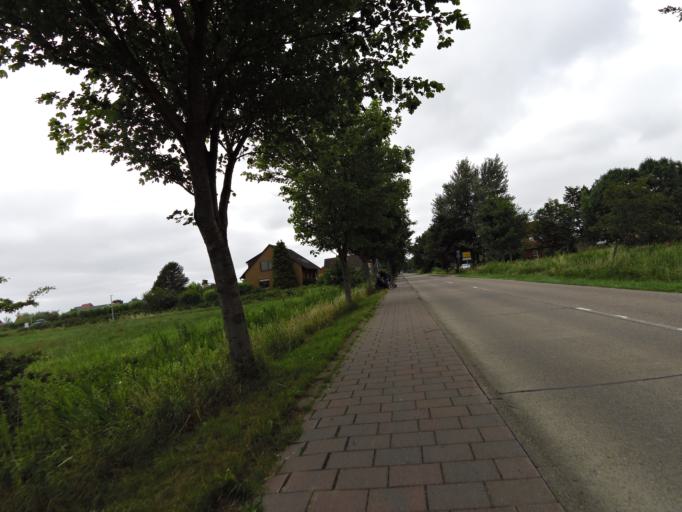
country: DE
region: Lower Saxony
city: Padingbuttel
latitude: 53.7307
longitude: 8.5287
